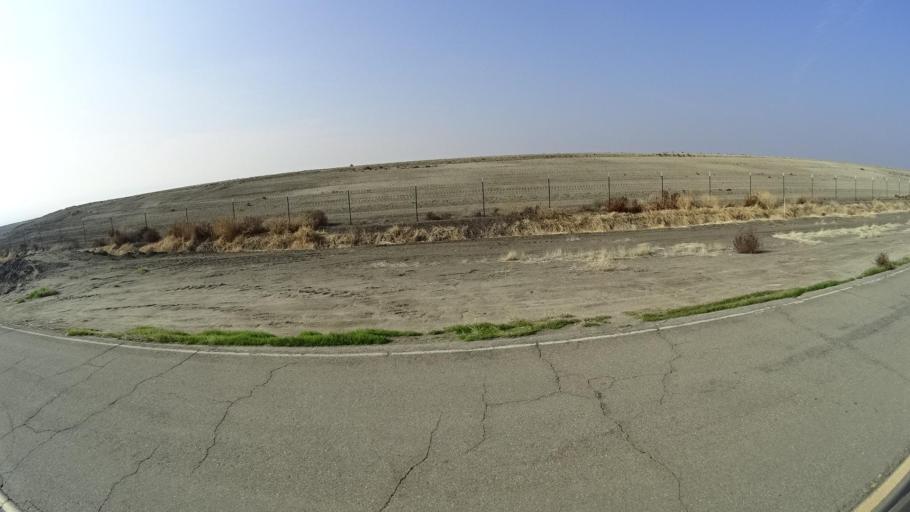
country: US
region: California
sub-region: Kern County
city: Buttonwillow
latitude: 35.3336
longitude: -119.3768
